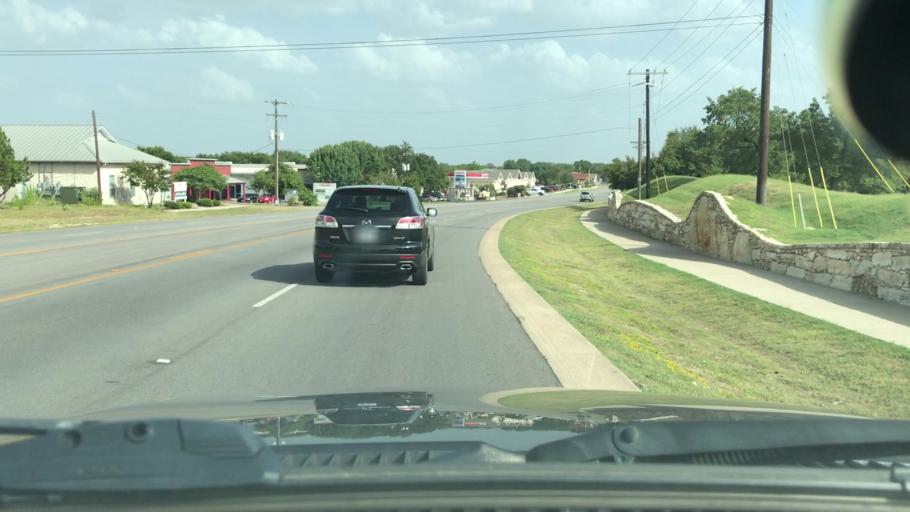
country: US
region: Texas
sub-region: Williamson County
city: Leander
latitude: 30.5506
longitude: -97.8542
